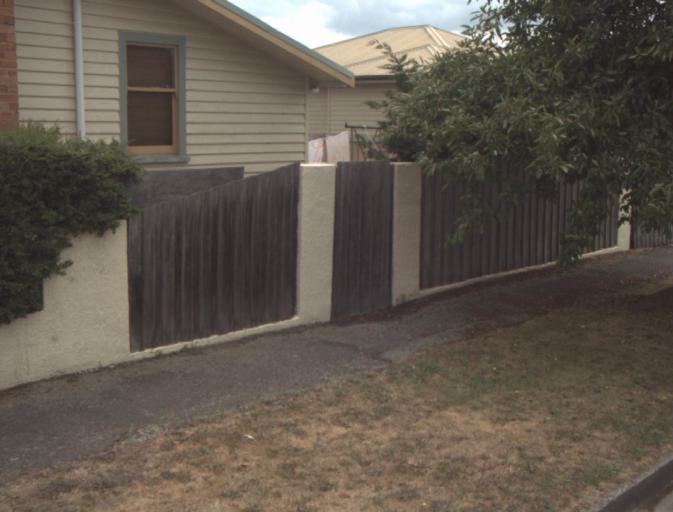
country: AU
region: Tasmania
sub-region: Launceston
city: Newnham
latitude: -41.4036
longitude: 147.1271
